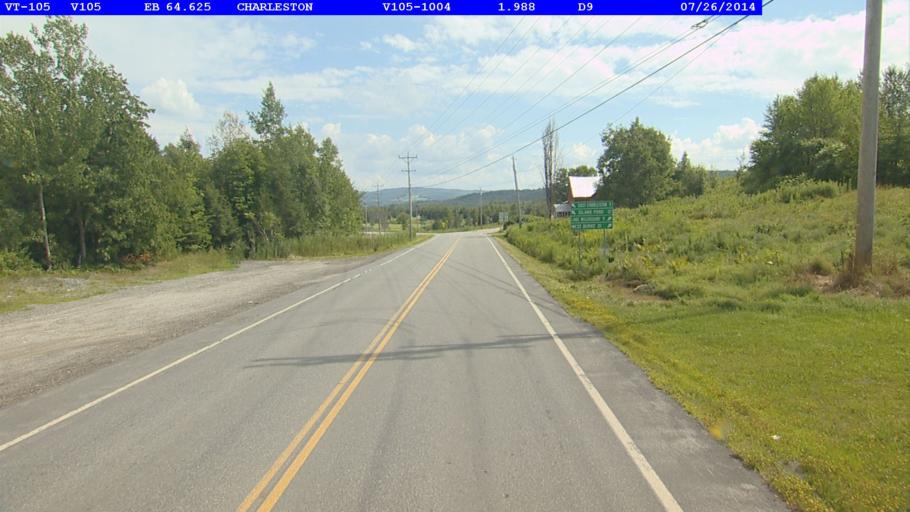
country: US
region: Vermont
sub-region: Orleans County
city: Newport
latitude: 44.8864
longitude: -72.0565
